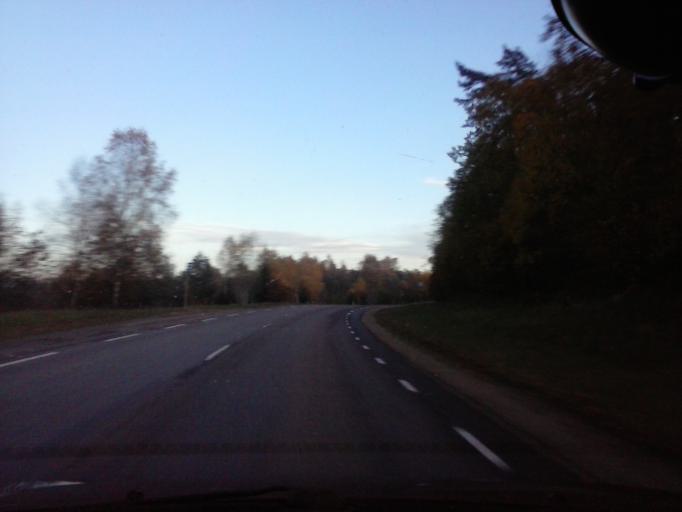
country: EE
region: Harju
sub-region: Nissi vald
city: Turba
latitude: 58.9162
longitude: 24.1946
